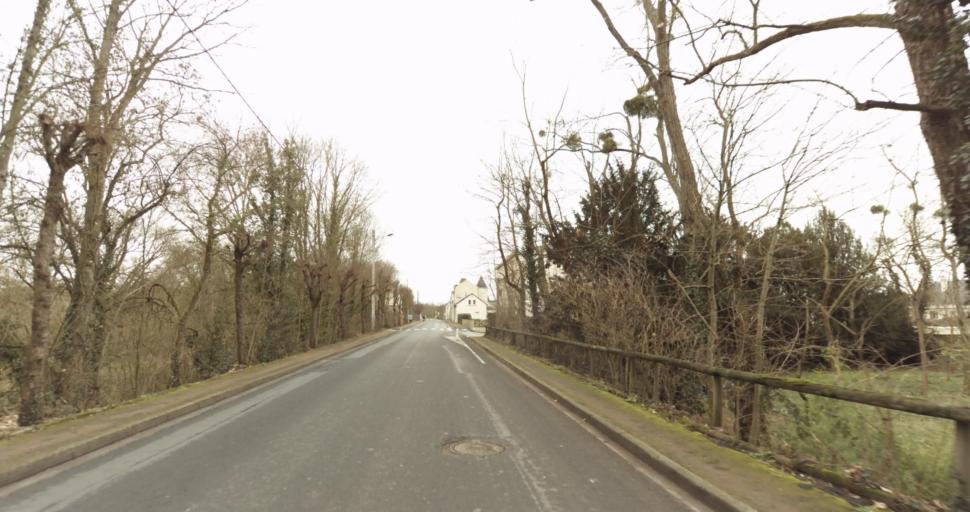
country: FR
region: Pays de la Loire
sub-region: Departement de Maine-et-Loire
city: Saumur
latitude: 47.2534
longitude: -0.0898
